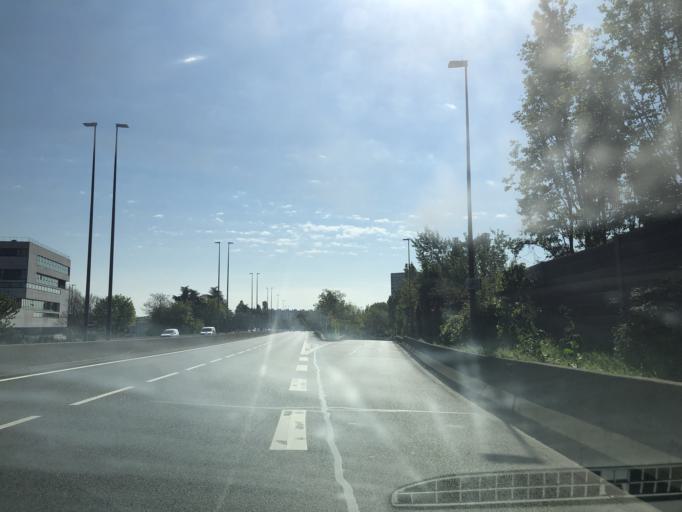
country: FR
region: Ile-de-France
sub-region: Departement du Val-de-Marne
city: Maisons-Alfort
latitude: 48.7928
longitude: 2.4436
